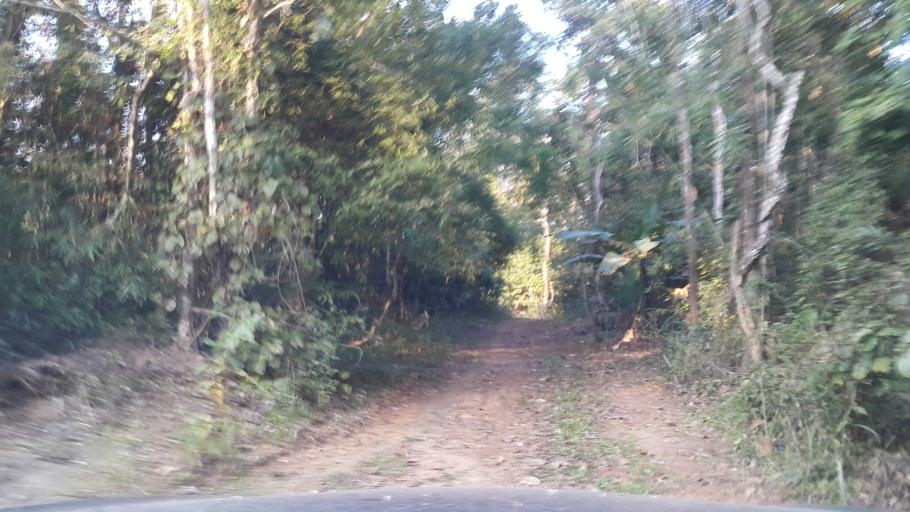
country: TH
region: Chiang Mai
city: Samoeng
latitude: 18.9056
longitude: 98.8611
